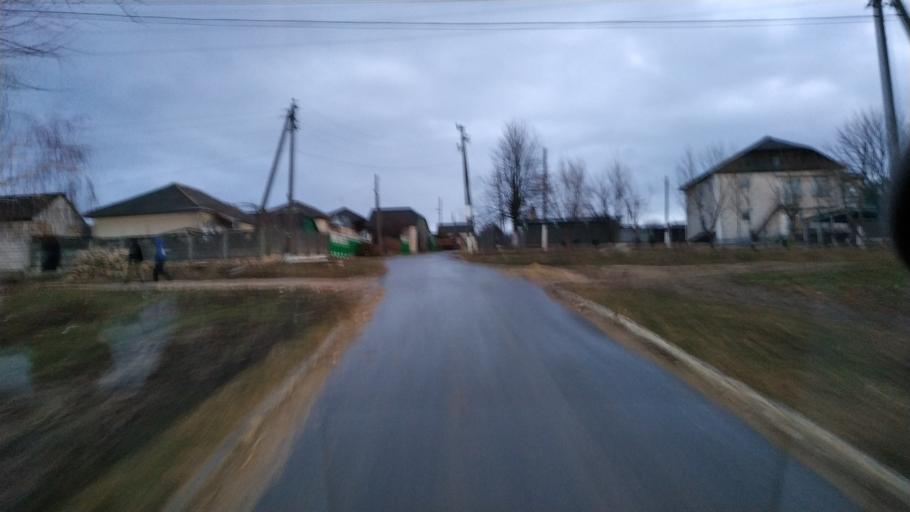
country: MD
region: Taraclia
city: Telenesti
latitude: 47.3725
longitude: 28.3778
